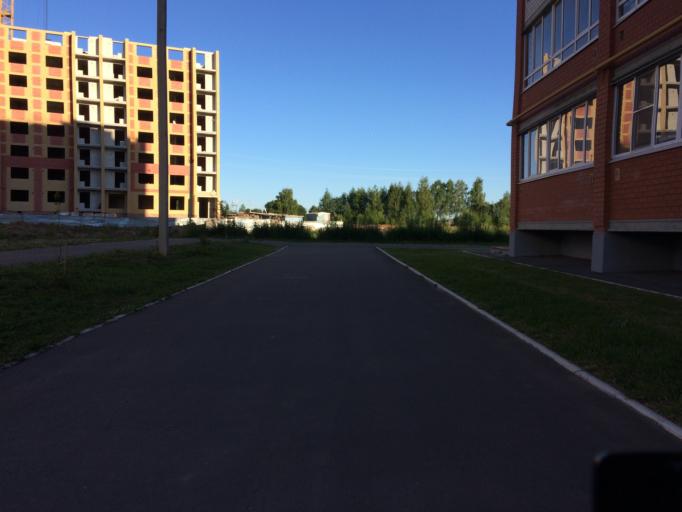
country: RU
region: Mariy-El
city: Medvedevo
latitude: 56.6486
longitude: 47.8342
